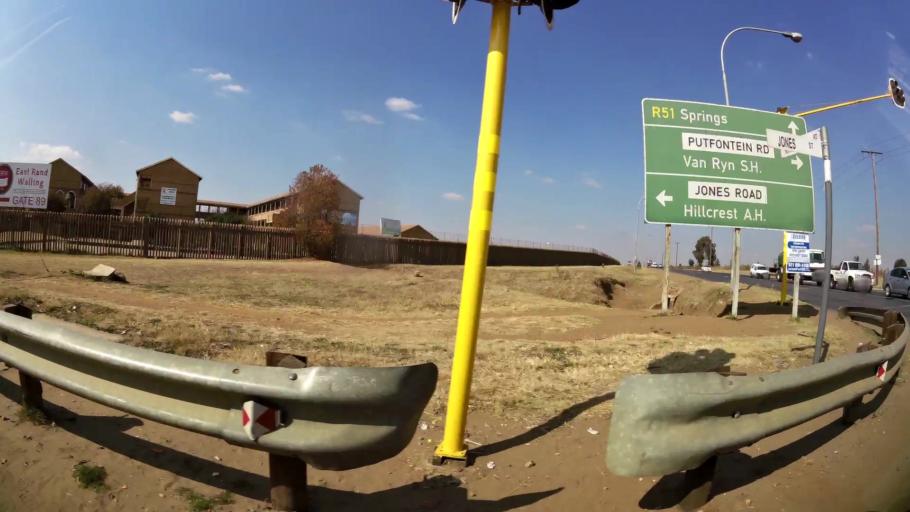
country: ZA
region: Gauteng
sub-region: Ekurhuleni Metropolitan Municipality
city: Benoni
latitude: -26.1388
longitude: 28.3917
